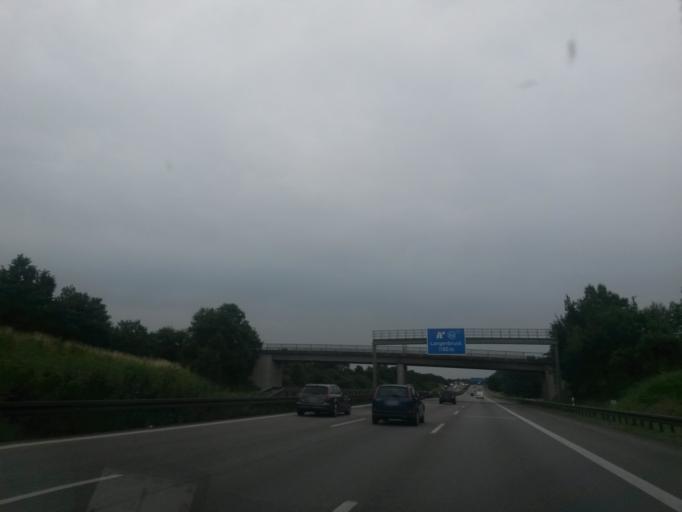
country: DE
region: Bavaria
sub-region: Upper Bavaria
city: Reichertshofen
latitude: 48.6598
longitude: 11.5117
